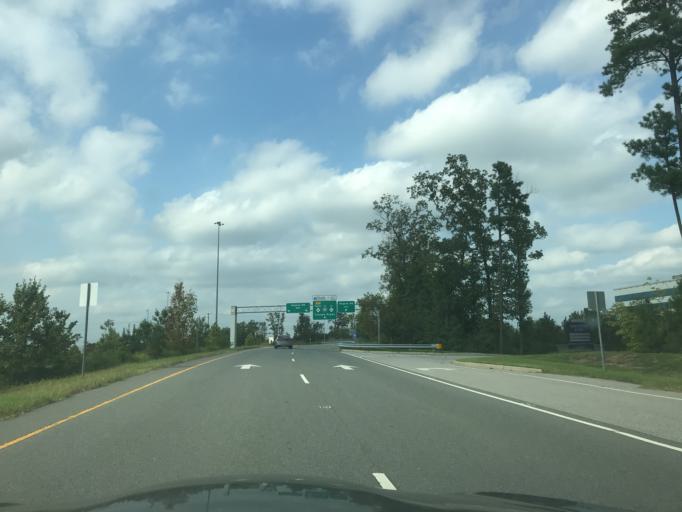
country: US
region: North Carolina
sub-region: Wake County
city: Morrisville
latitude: 35.8744
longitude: -78.8656
